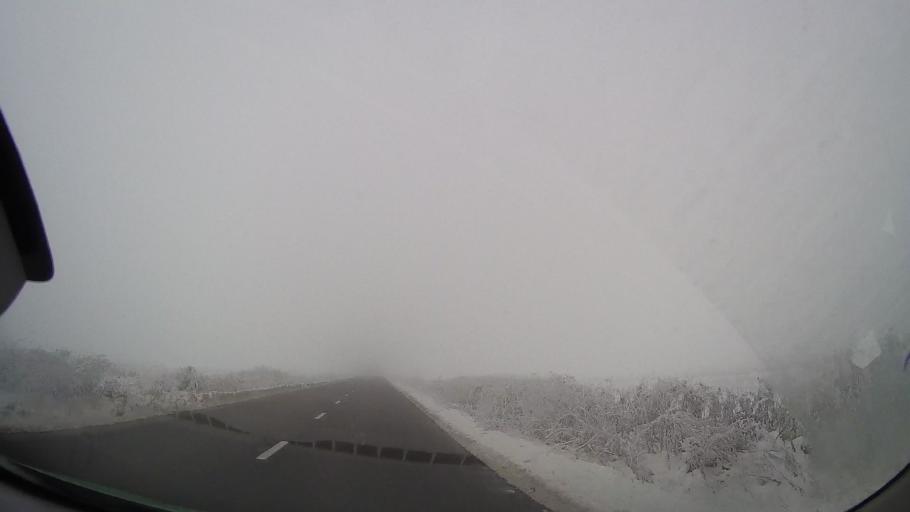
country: RO
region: Iasi
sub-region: Comuna Mircesti
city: Iugani
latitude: 47.0410
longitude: 26.8515
